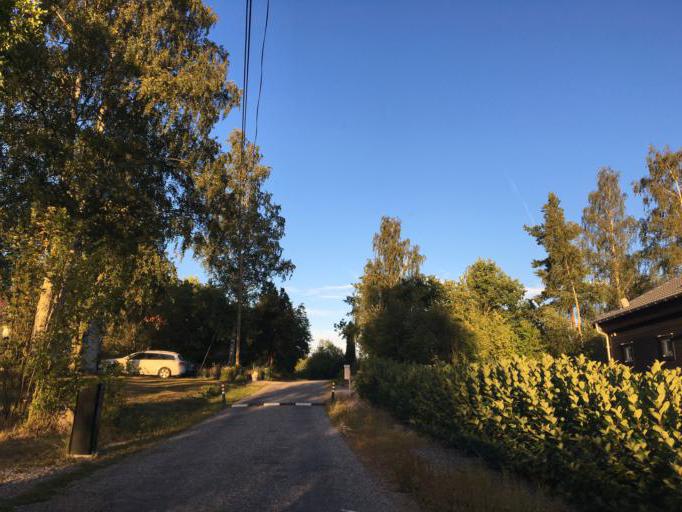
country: SE
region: Soedermanland
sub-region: Eskilstuna Kommun
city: Torshalla
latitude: 59.4328
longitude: 16.4481
